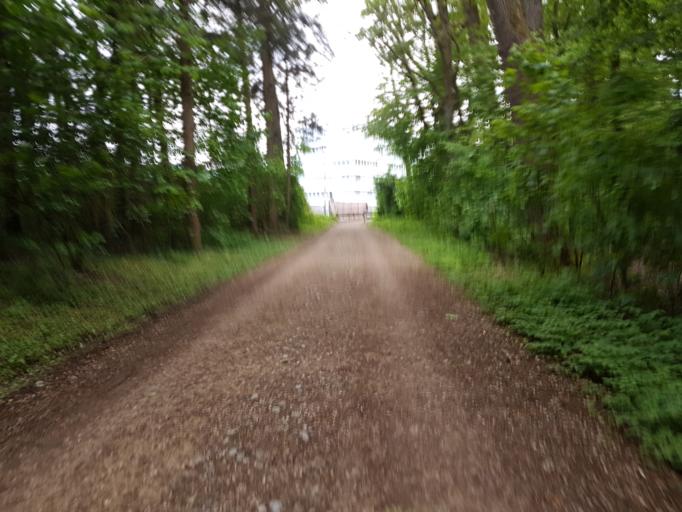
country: CH
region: Solothurn
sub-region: Bezirk Goesgen
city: Niedererlinsbach
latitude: 47.3831
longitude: 8.0102
